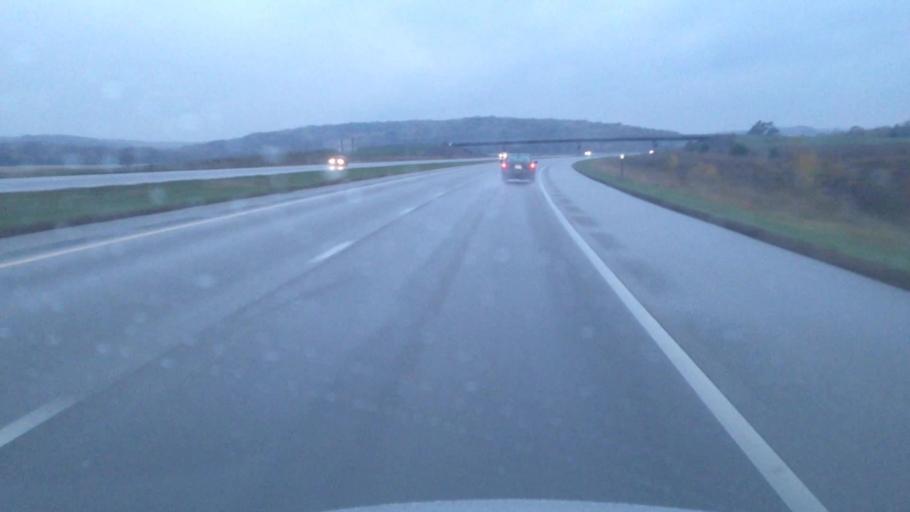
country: US
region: Kansas
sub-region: Douglas County
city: Lawrence
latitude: 38.8735
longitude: -95.2558
